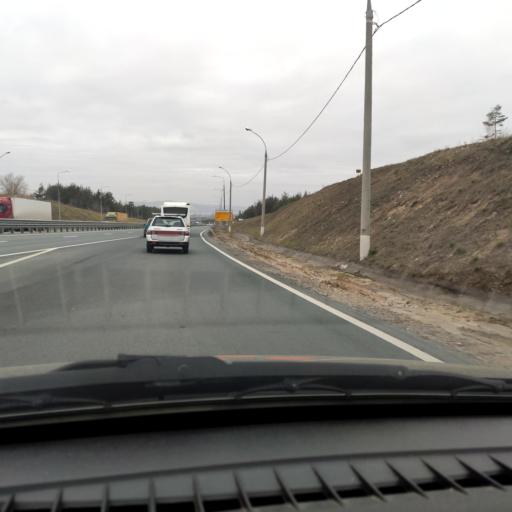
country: RU
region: Samara
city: Zhigulevsk
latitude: 53.4983
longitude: 49.5375
